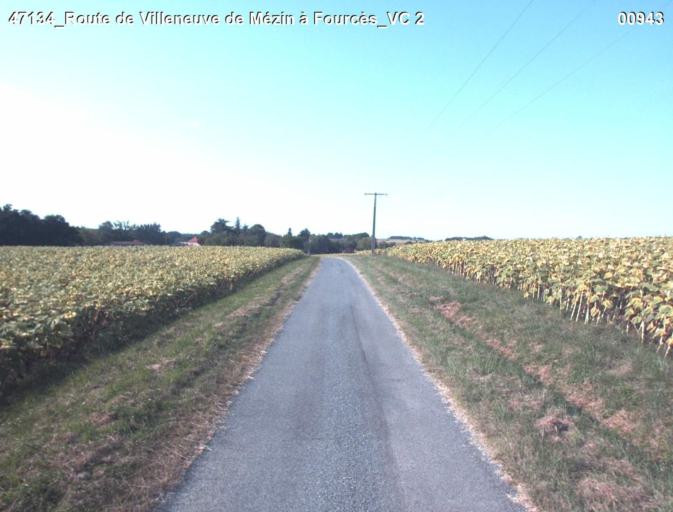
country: FR
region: Aquitaine
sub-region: Departement du Lot-et-Garonne
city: Mezin
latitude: 44.0094
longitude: 0.2483
